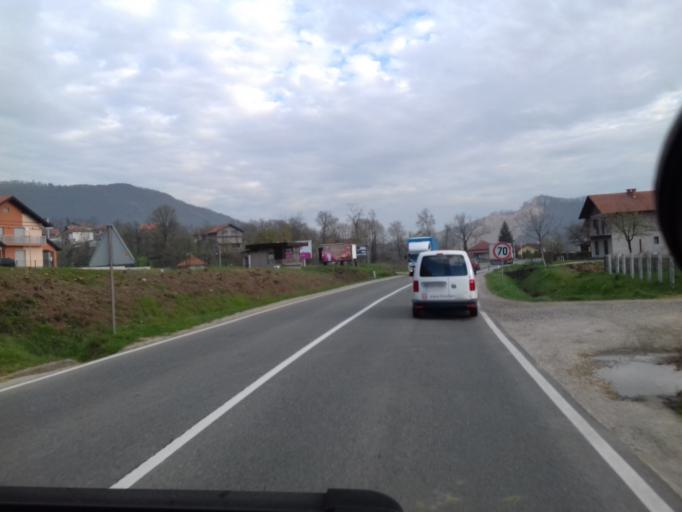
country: BA
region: Federation of Bosnia and Herzegovina
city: Maglaj
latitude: 44.6149
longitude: 18.0978
